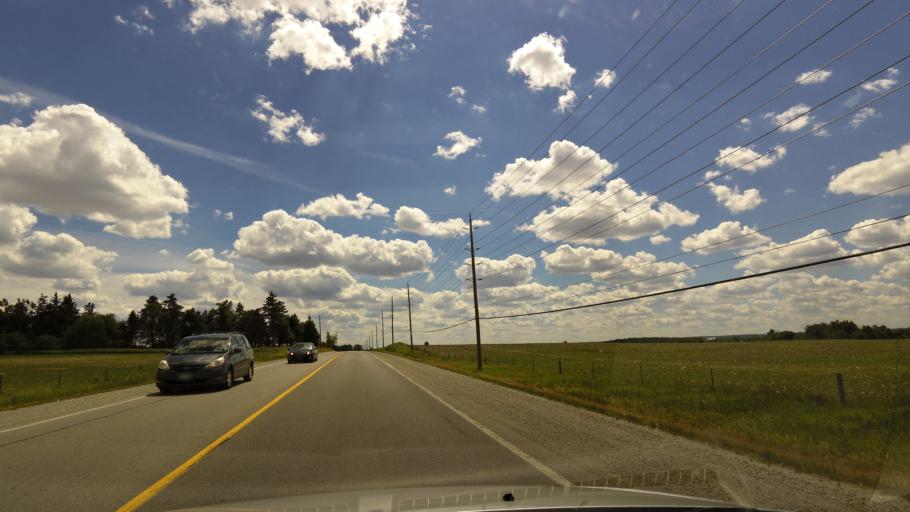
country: CA
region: Ontario
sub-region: Halton
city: Milton
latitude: 43.6148
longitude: -79.8873
